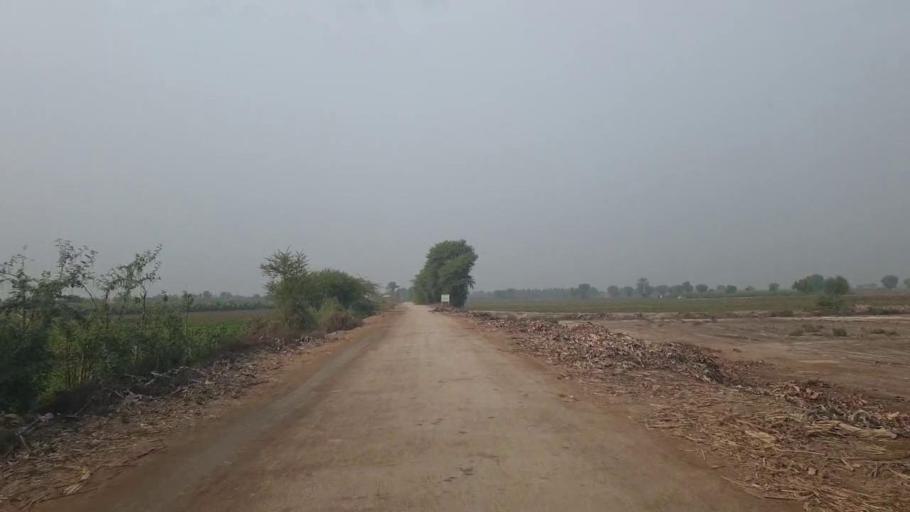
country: PK
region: Sindh
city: Tando Adam
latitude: 25.8096
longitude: 68.7189
